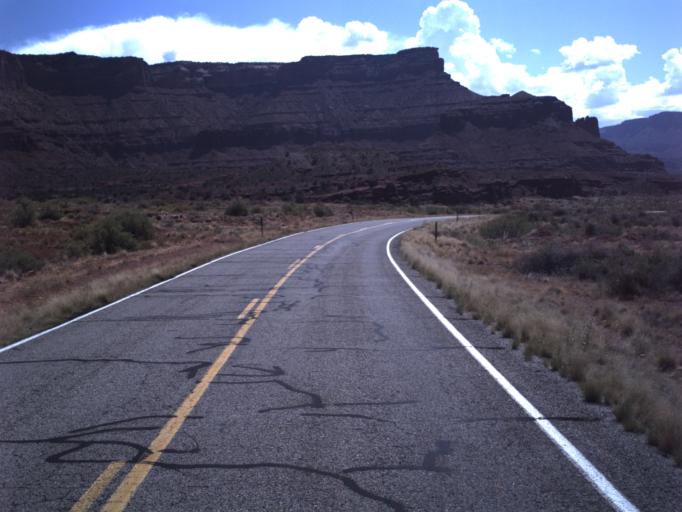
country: US
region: Utah
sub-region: Grand County
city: Moab
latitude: 38.7680
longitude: -109.3209
